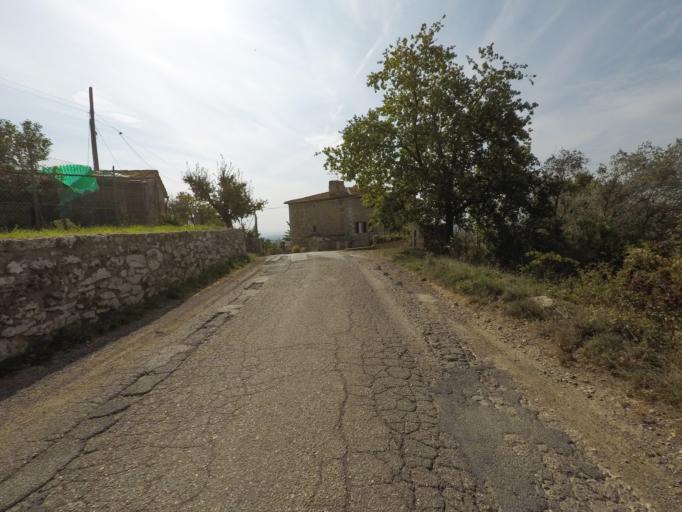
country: IT
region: Tuscany
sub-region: Provincia di Siena
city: Castellina in Chianti
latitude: 43.4205
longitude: 11.3399
